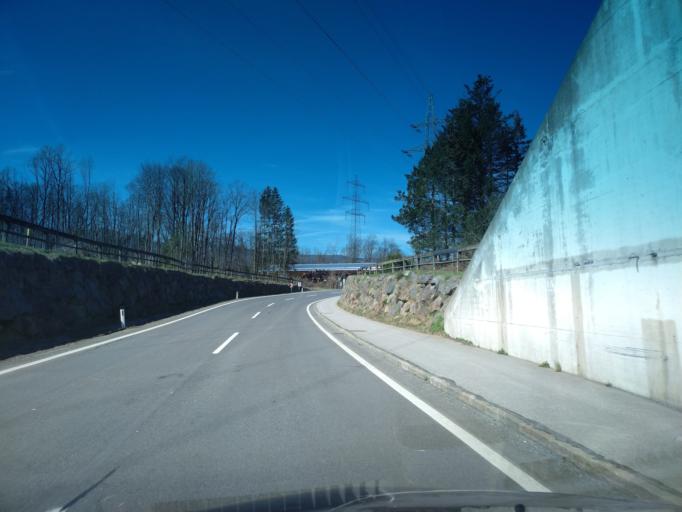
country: AT
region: Styria
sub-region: Politischer Bezirk Deutschlandsberg
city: Hollenegg
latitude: 46.7930
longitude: 15.2351
